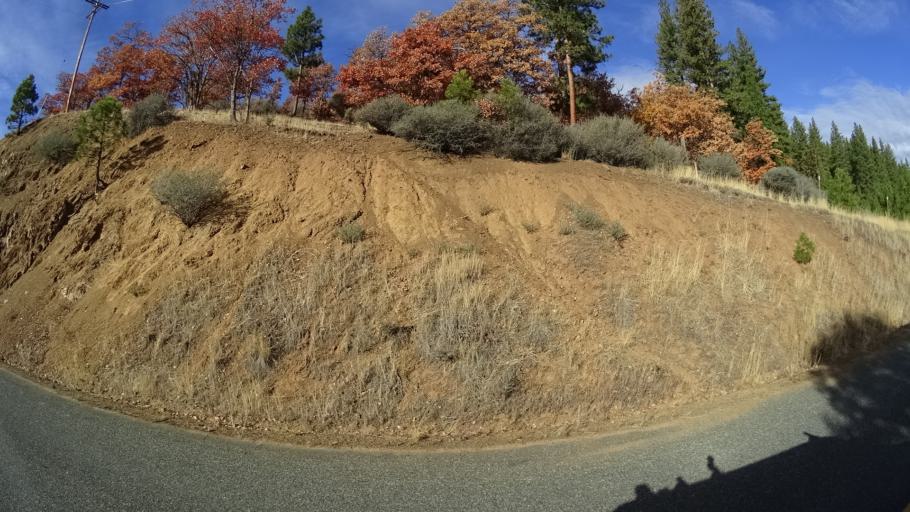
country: US
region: California
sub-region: Siskiyou County
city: Yreka
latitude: 41.6612
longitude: -122.8350
